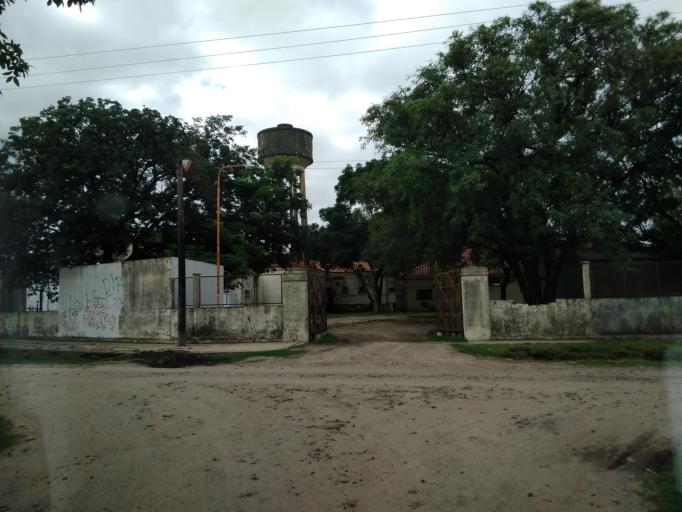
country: AR
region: Corrientes
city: Corrientes
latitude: -27.4733
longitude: -58.8109
